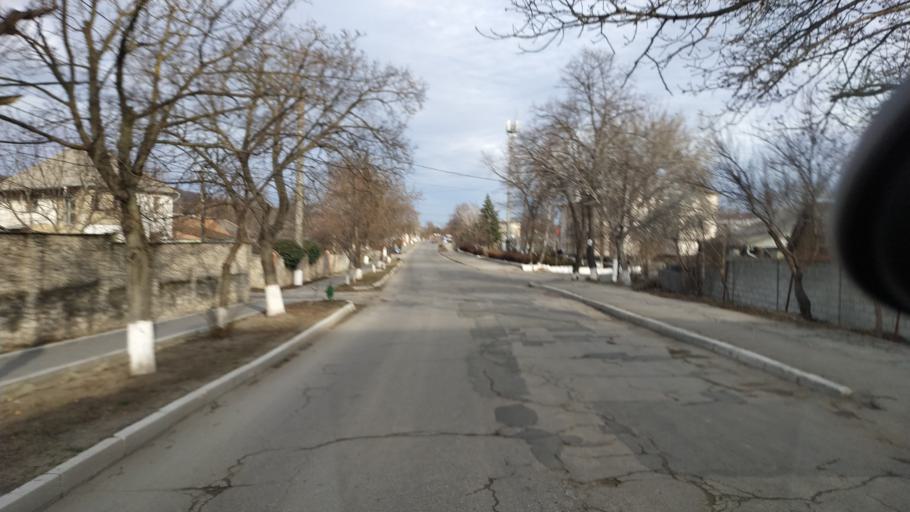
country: MD
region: Chisinau
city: Vadul lui Voda
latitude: 47.0911
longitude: 29.0766
